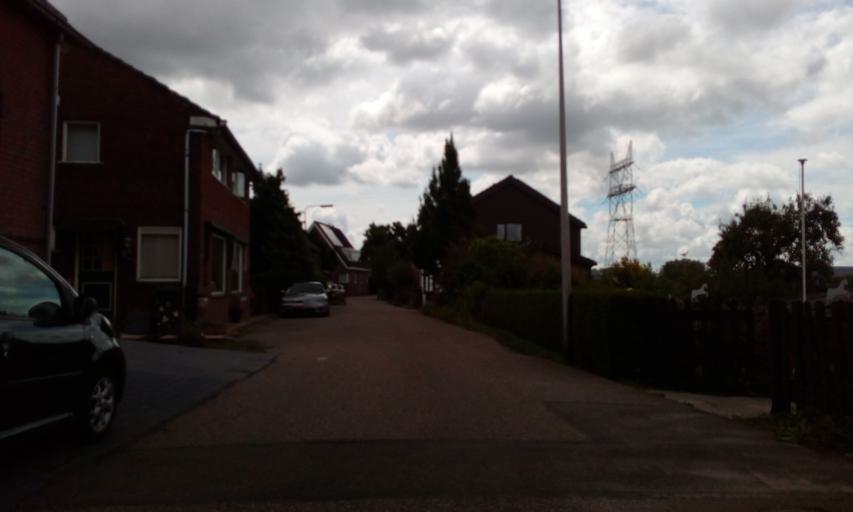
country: NL
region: South Holland
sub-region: Gemeente Barendrecht
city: Barendrecht
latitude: 51.8703
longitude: 4.5432
